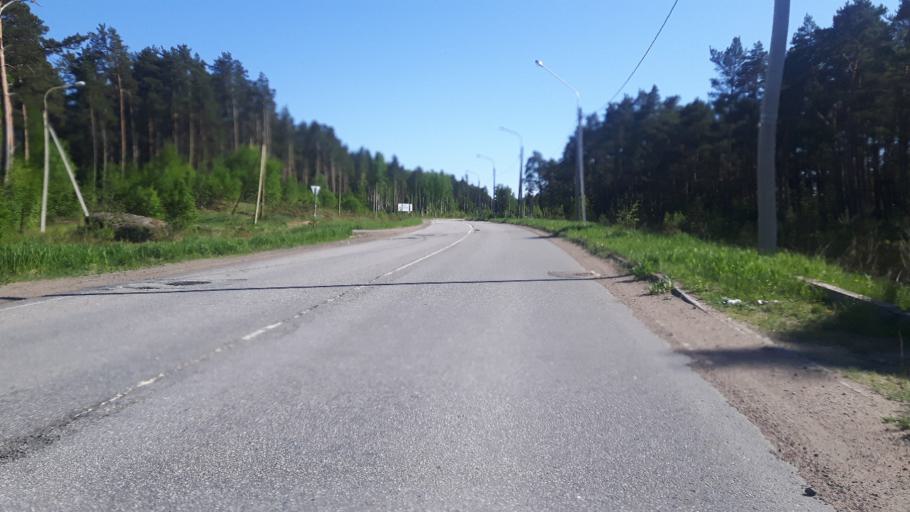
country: RU
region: Leningrad
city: Sosnovyy Bor
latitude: 60.2026
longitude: 29.0062
